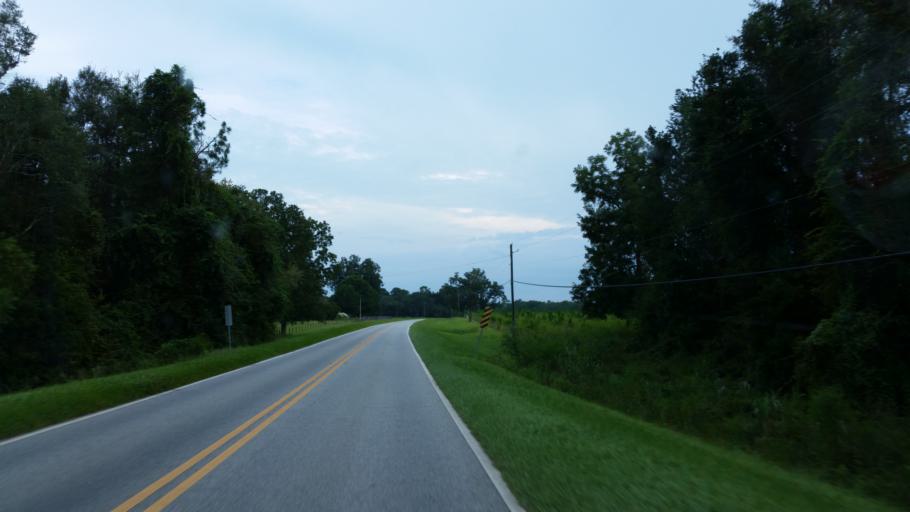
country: US
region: Georgia
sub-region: Lowndes County
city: Valdosta
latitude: 30.7693
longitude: -83.3035
